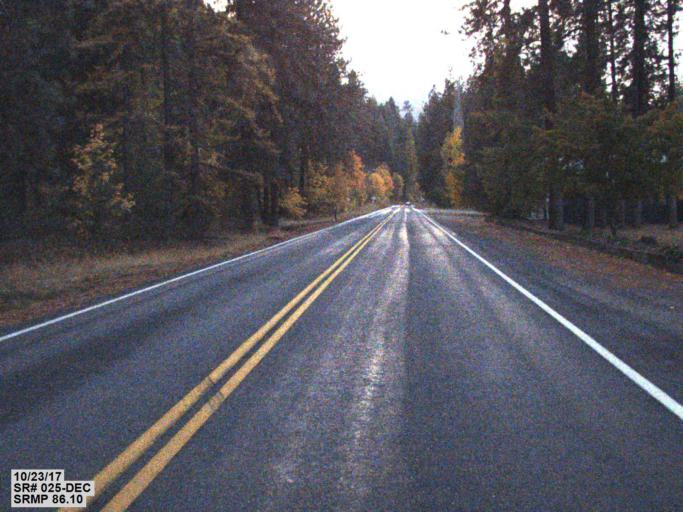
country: US
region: Washington
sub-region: Stevens County
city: Kettle Falls
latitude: 48.6632
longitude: -118.0642
